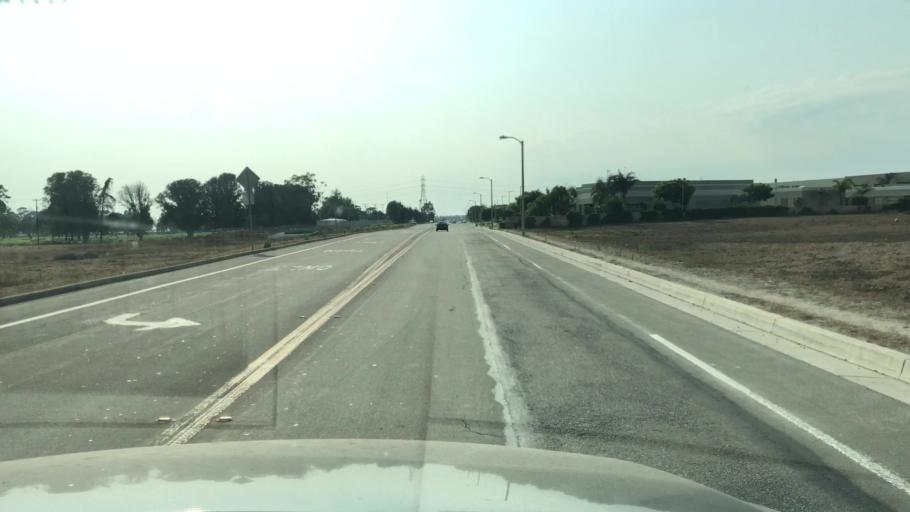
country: US
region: California
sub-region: Ventura County
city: El Rio
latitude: 34.2413
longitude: -119.2036
